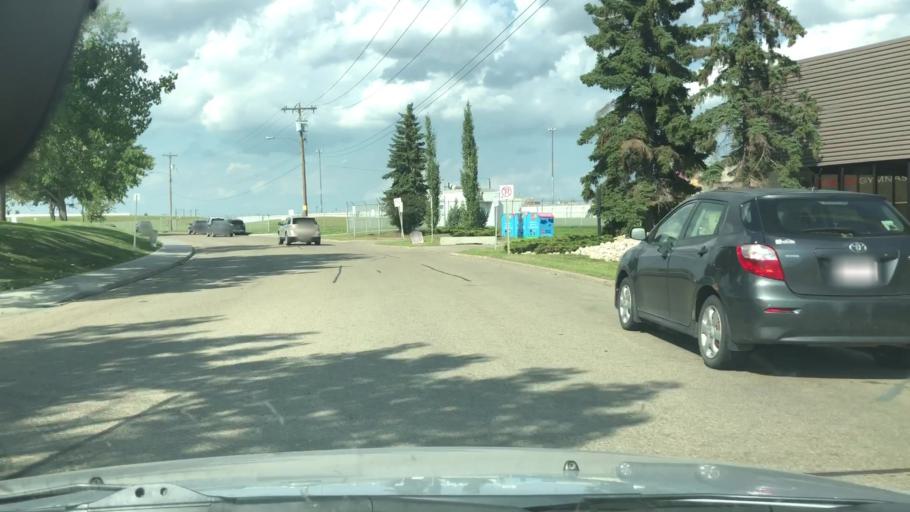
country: CA
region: Alberta
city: Edmonton
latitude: 53.5357
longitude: -113.4144
